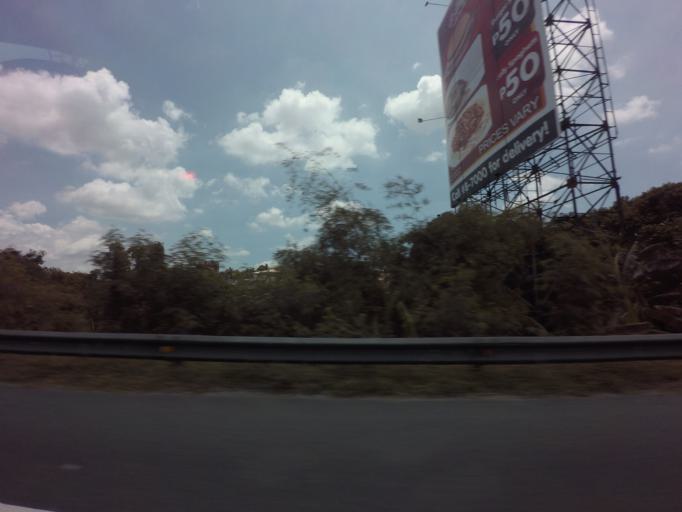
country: PH
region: Calabarzon
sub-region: Province of Laguna
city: San Pedro
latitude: 14.4026
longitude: 121.0394
